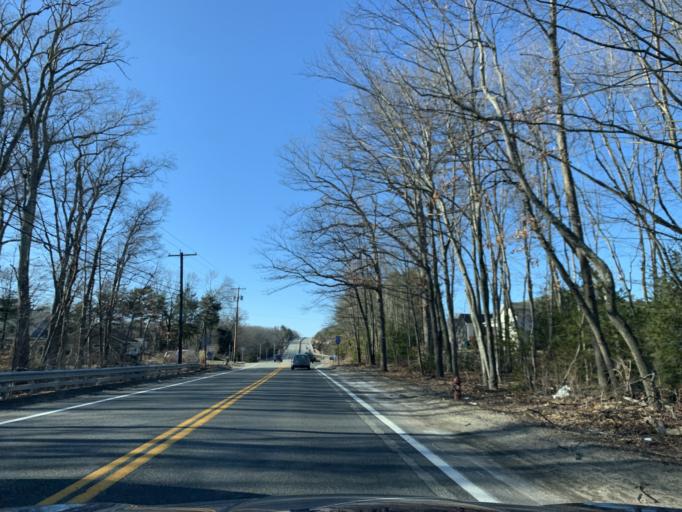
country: US
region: Rhode Island
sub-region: Providence County
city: Smithfield
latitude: 41.9038
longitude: -71.5065
